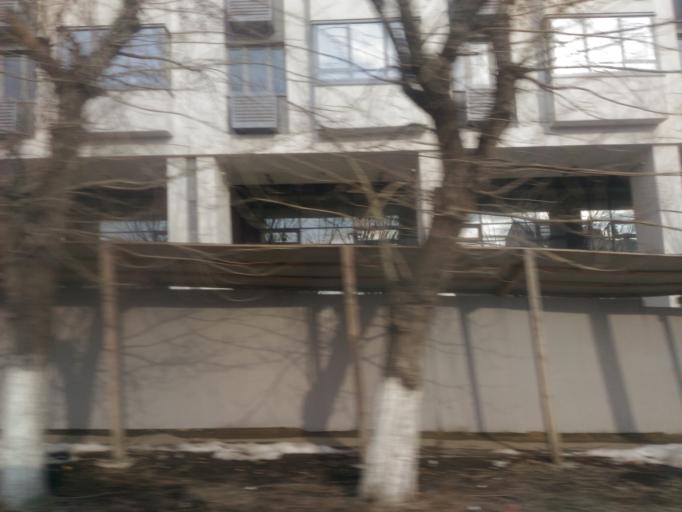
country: RU
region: Ulyanovsk
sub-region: Ulyanovskiy Rayon
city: Ulyanovsk
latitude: 54.3064
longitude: 48.3895
